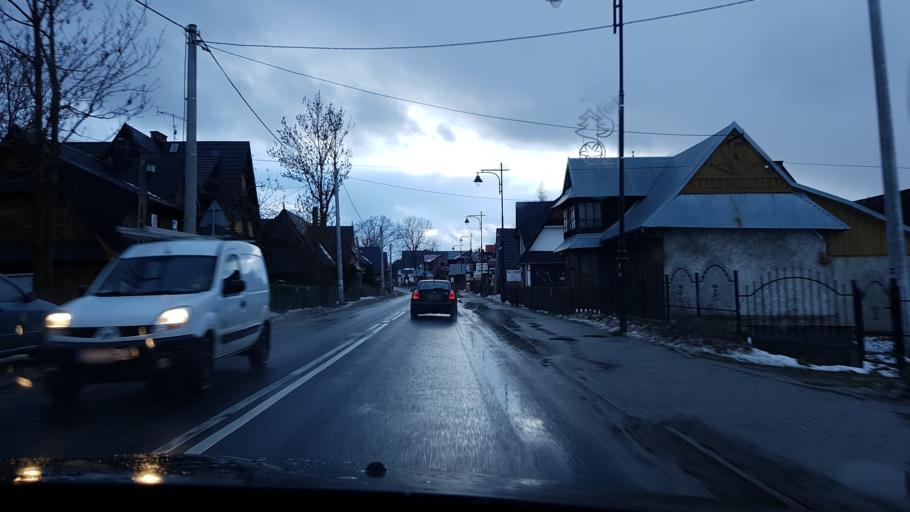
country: PL
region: Lesser Poland Voivodeship
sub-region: Powiat tatrzanski
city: Bukowina Tatrzanska
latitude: 49.3410
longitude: 20.1040
